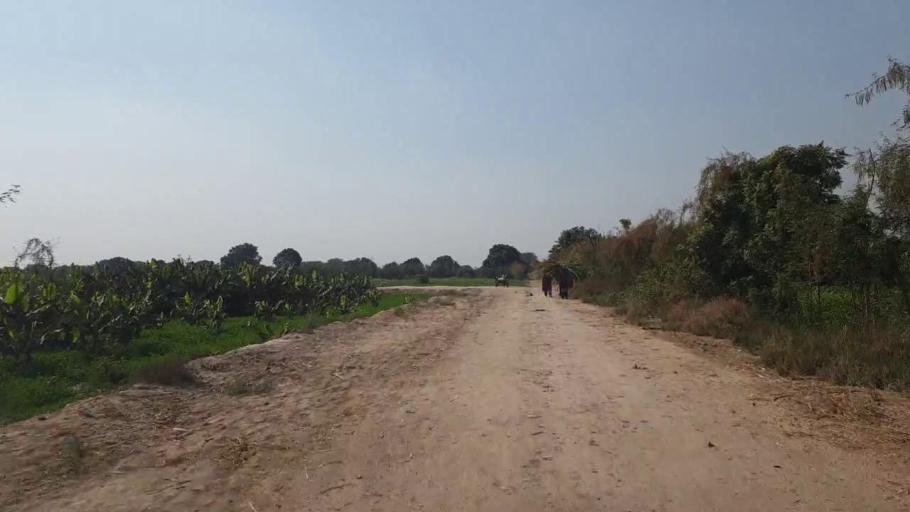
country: PK
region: Sindh
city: Chambar
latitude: 25.3768
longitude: 68.8766
